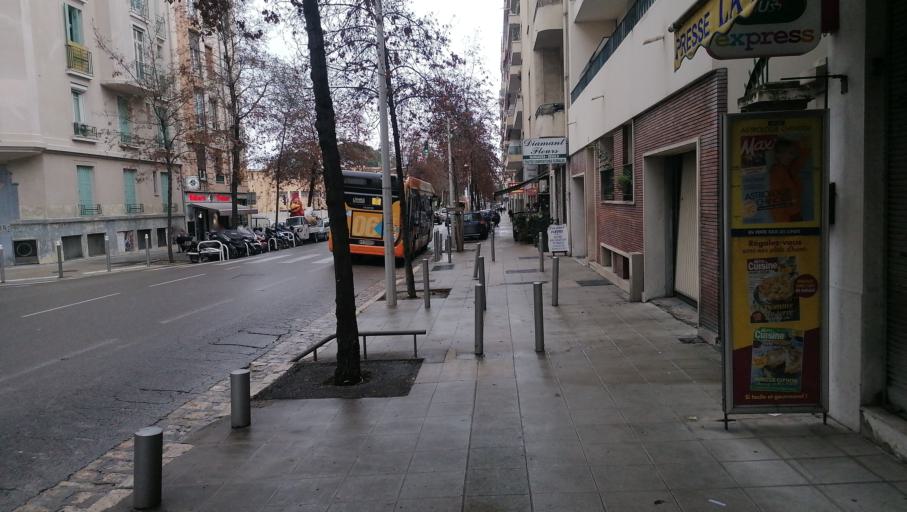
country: FR
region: Provence-Alpes-Cote d'Azur
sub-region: Departement des Alpes-Maritimes
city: Nice
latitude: 43.7167
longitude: 7.2534
